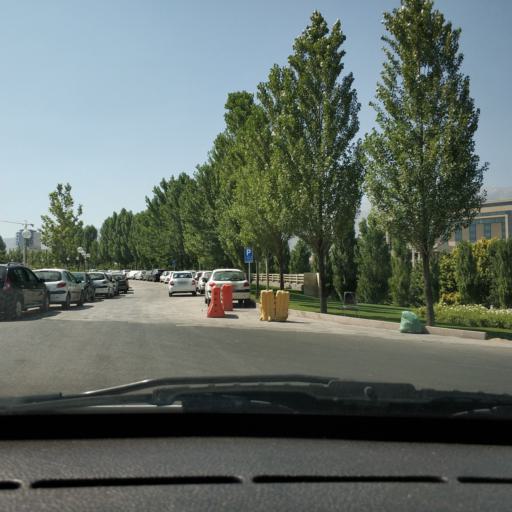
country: IR
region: Tehran
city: Tajrish
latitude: 35.7560
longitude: 51.4344
